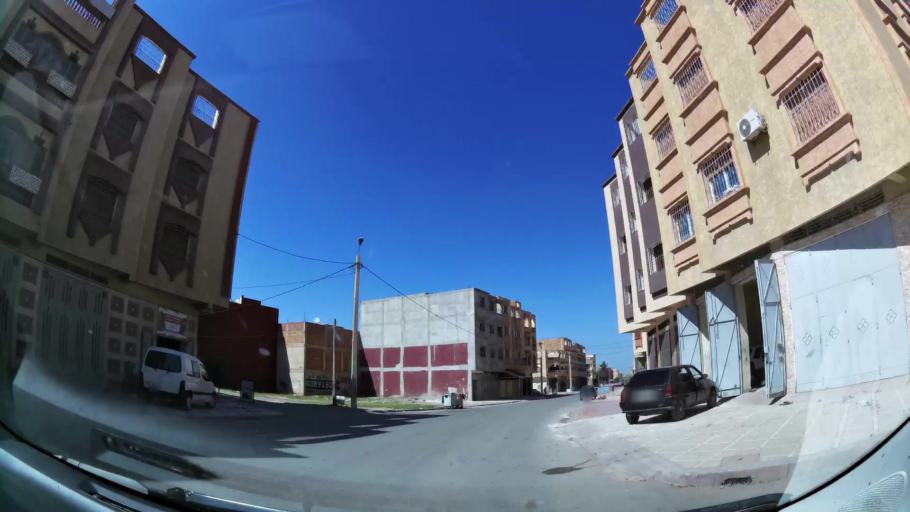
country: MA
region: Oriental
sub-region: Oujda-Angad
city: Oujda
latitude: 34.6848
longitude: -1.9425
